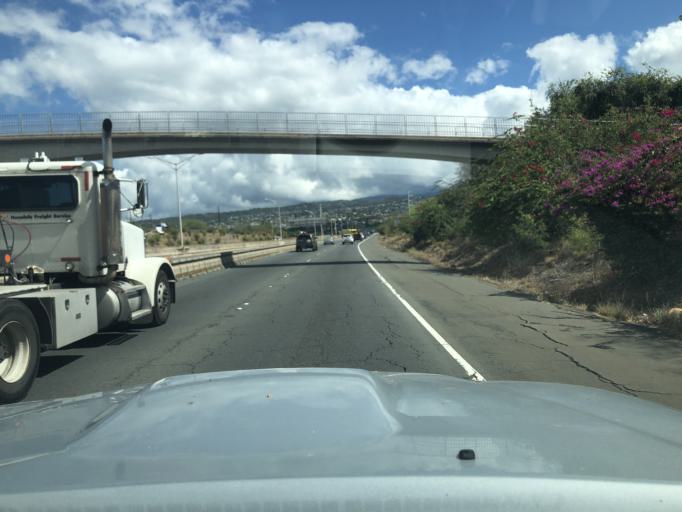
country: US
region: Hawaii
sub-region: Honolulu County
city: Halawa
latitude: 21.3604
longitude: -157.9306
